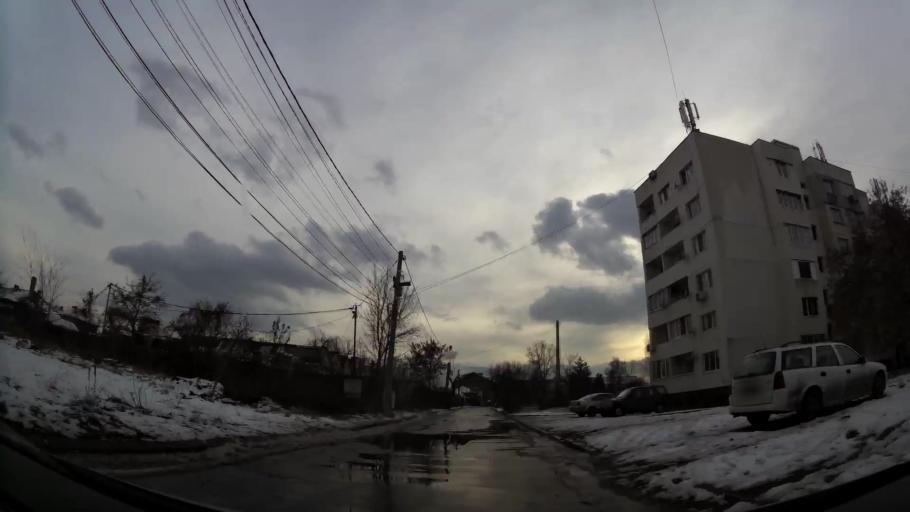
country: BG
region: Sofia-Capital
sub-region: Stolichna Obshtina
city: Sofia
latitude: 42.7231
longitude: 23.3368
